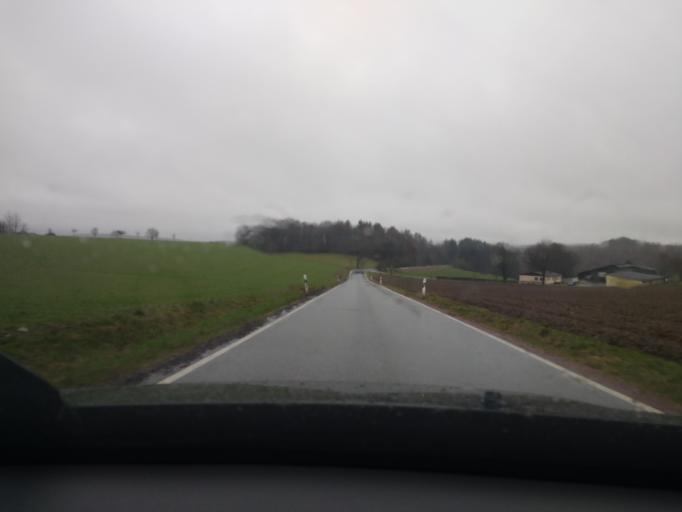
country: DE
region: Rheinland-Pfalz
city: Lampaden
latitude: 49.6523
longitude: 6.6925
